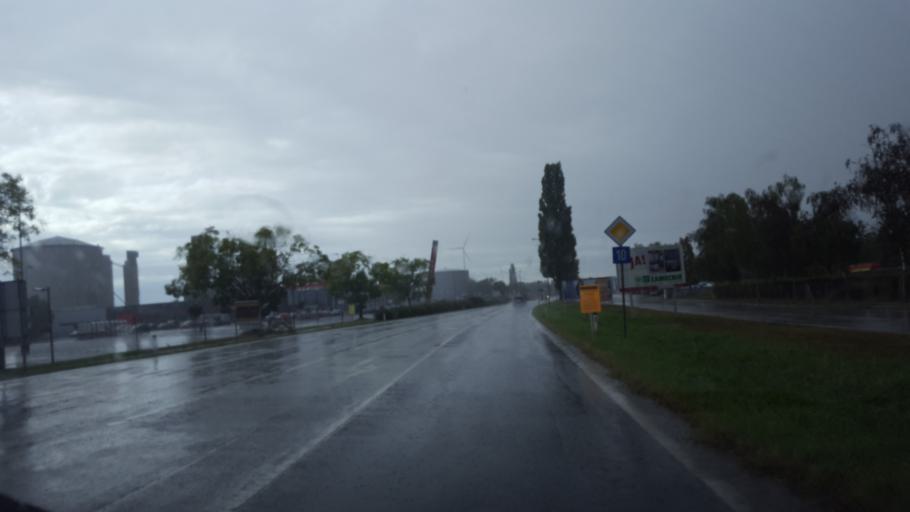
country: AT
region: Lower Austria
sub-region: Politischer Bezirk Bruck an der Leitha
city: Bruck an der Leitha
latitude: 48.0218
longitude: 16.7605
